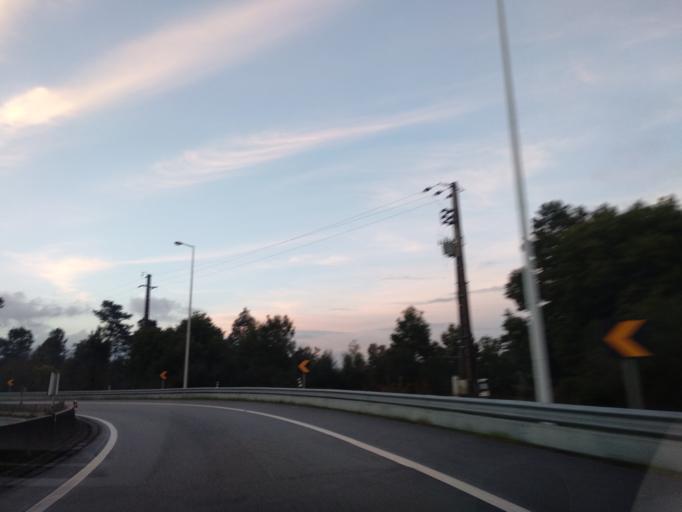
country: PT
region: Braga
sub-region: Vila Nova de Famalicao
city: Vila Nova de Famalicao
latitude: 41.3827
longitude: -8.5027
